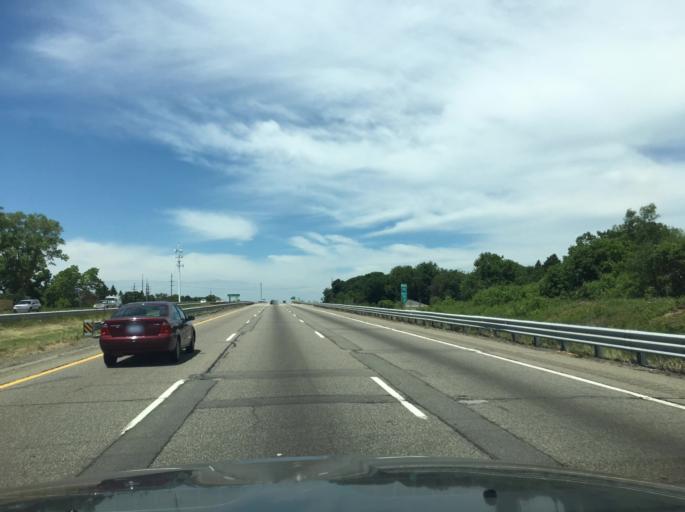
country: US
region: Michigan
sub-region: Oakland County
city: Bloomfield Hills
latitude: 42.6056
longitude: -83.2034
